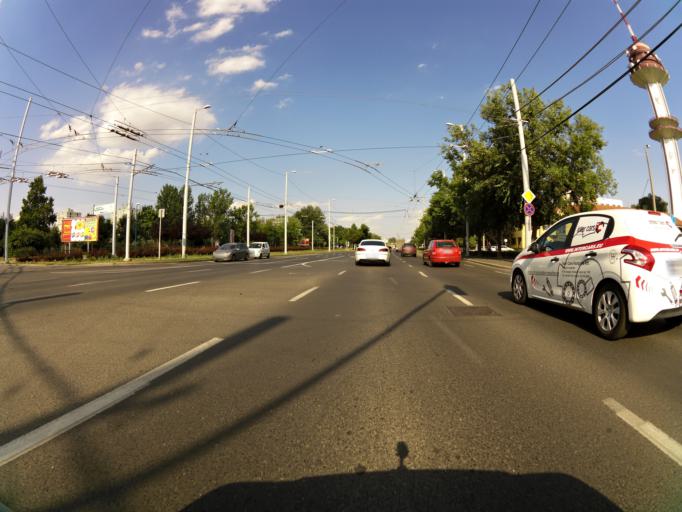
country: HU
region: Csongrad
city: Szeged
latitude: 46.2720
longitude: 20.1436
